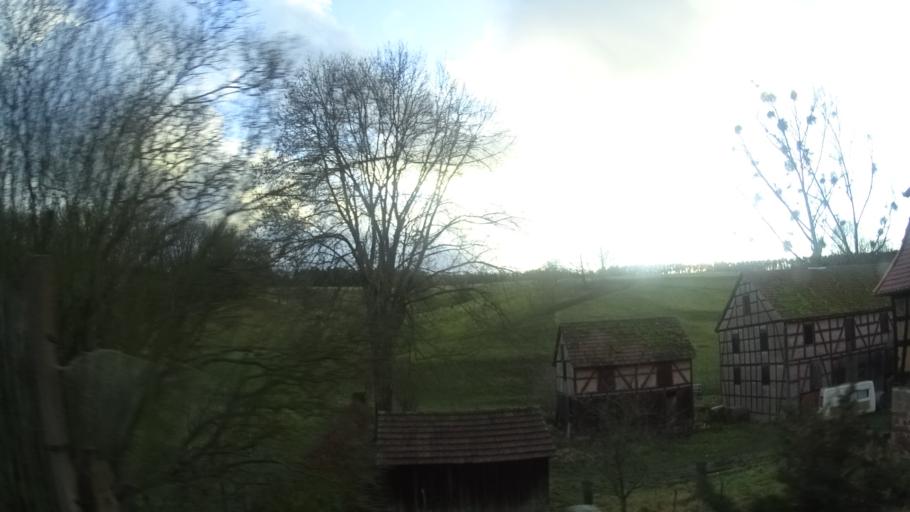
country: DE
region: Thuringia
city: Unterwellenborn
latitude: 50.6855
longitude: 11.4356
